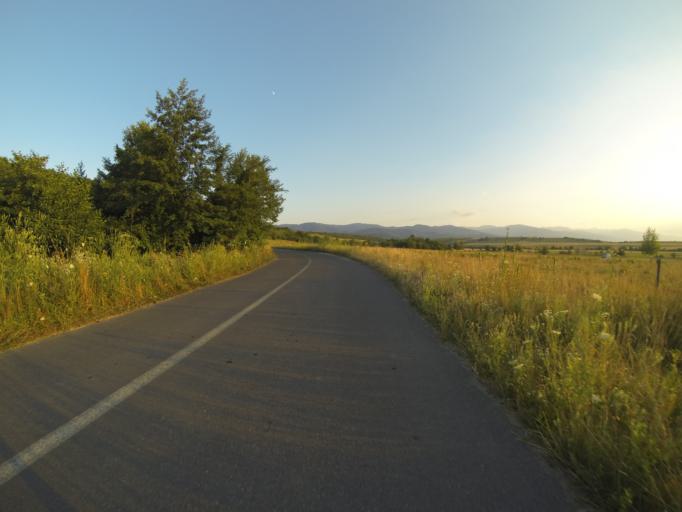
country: RO
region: Brasov
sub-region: Comuna Sinca Veche
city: Sinca Veche
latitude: 45.7539
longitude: 25.1650
